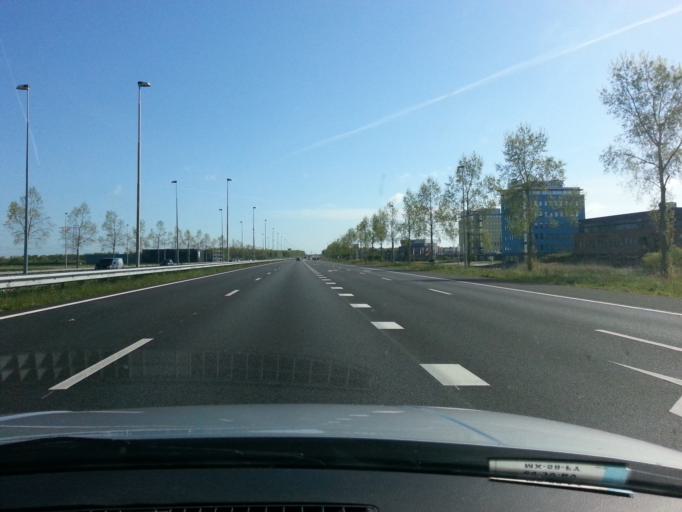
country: NL
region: Flevoland
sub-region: Gemeente Lelystad
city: Lelystad
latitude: 52.4724
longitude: 5.4872
